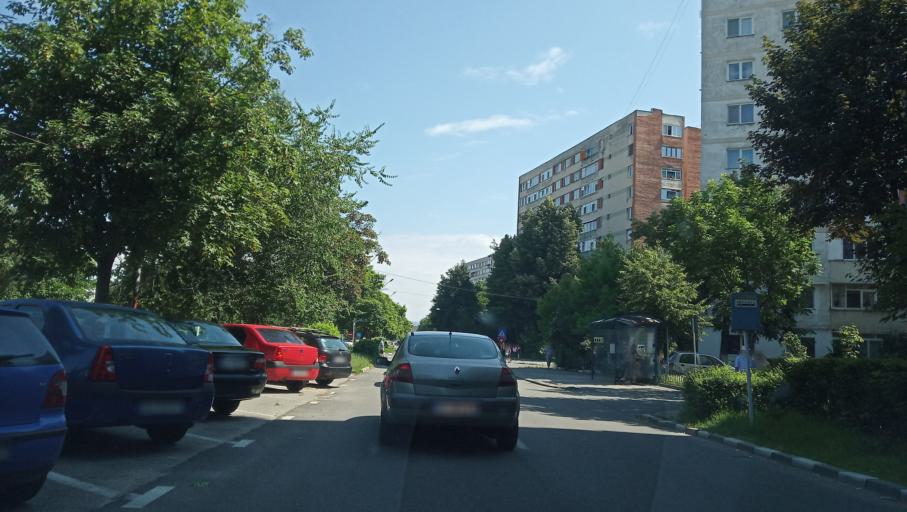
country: RO
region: Valcea
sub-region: Municipiul Ramnicu Valcea
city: Ramnicu Valcea
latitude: 45.0942
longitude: 24.3657
